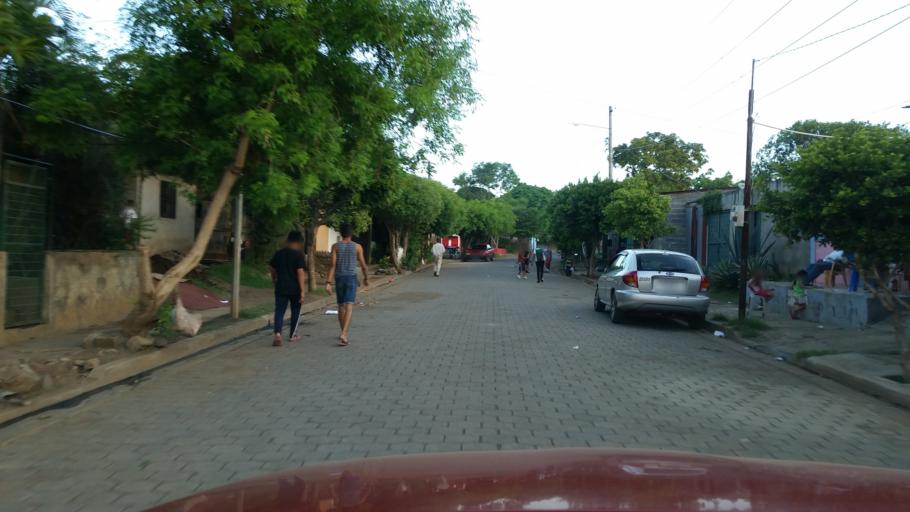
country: NI
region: Managua
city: Managua
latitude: 12.1347
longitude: -86.2871
